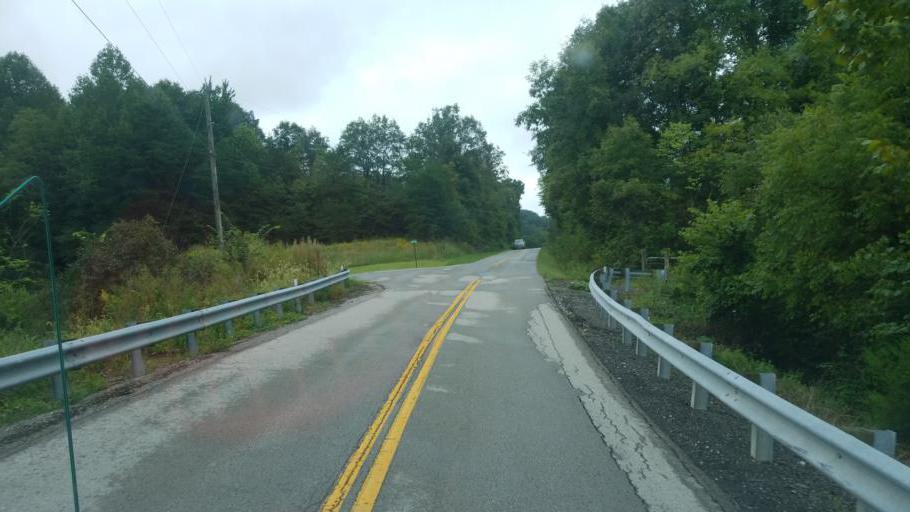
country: US
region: Kentucky
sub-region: Fleming County
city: Flemingsburg
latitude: 38.3837
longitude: -83.5428
